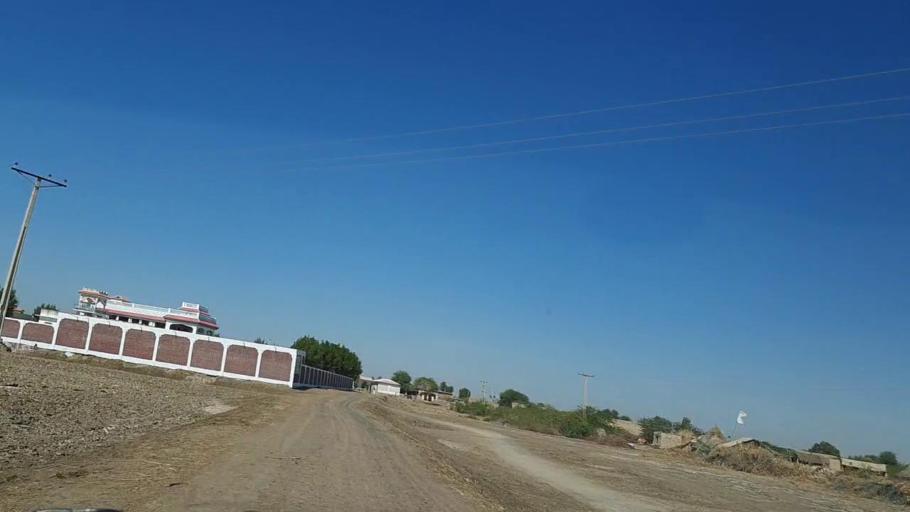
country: PK
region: Sindh
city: Dhoro Naro
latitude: 25.5307
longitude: 69.5016
